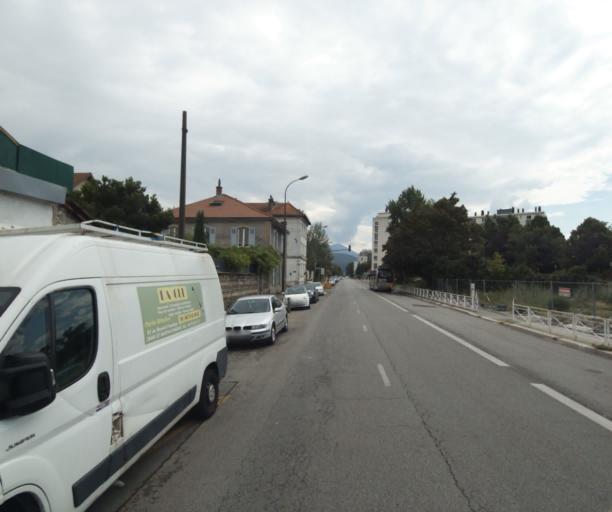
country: FR
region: Rhone-Alpes
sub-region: Departement de l'Isere
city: Grenoble
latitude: 45.1776
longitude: 5.7365
